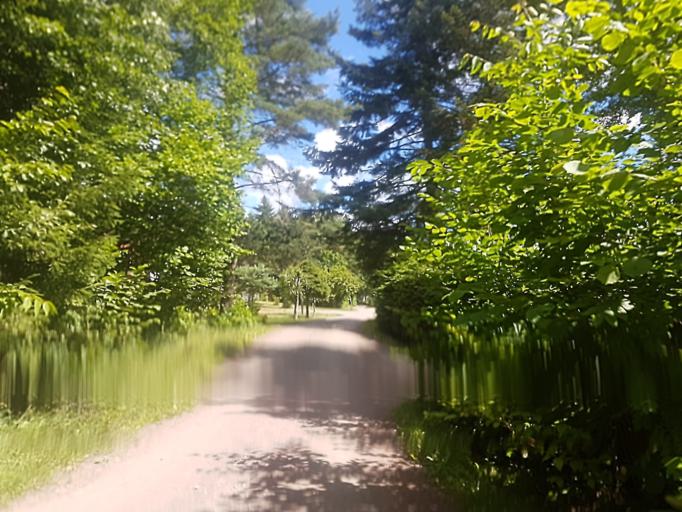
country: SE
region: Soedermanland
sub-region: Gnesta Kommun
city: Gnesta
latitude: 59.0339
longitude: 17.3452
